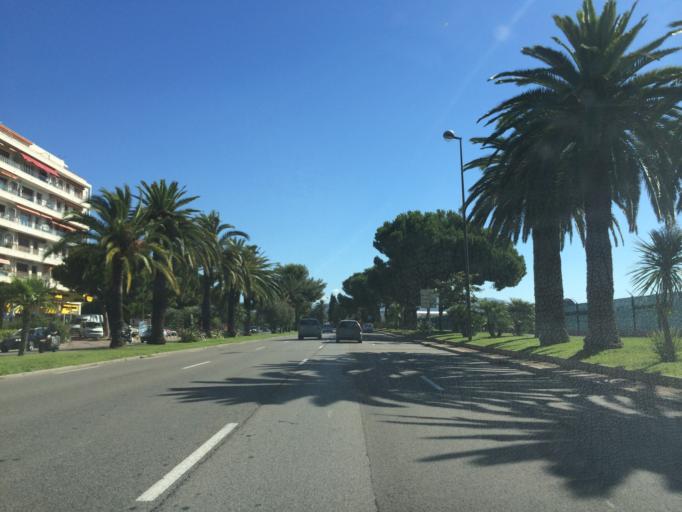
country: FR
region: Provence-Alpes-Cote d'Azur
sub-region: Departement des Alpes-Maritimes
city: Saint-Laurent-du-Var
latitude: 43.6708
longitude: 7.2239
